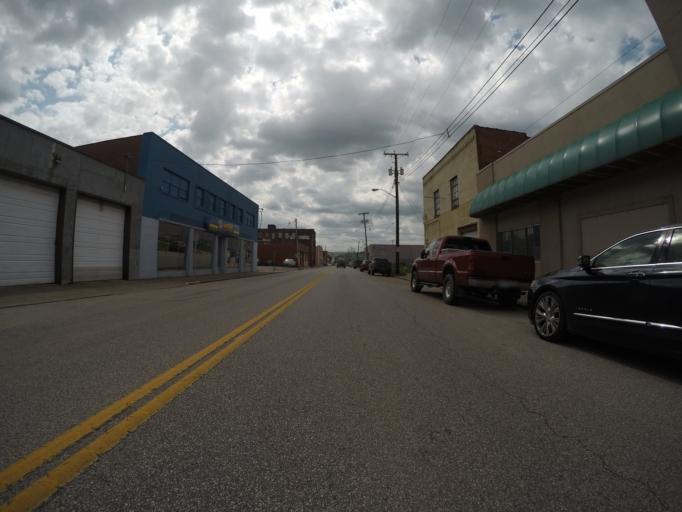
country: US
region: West Virginia
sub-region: Kanawha County
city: Charleston
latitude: 38.3633
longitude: -81.6500
